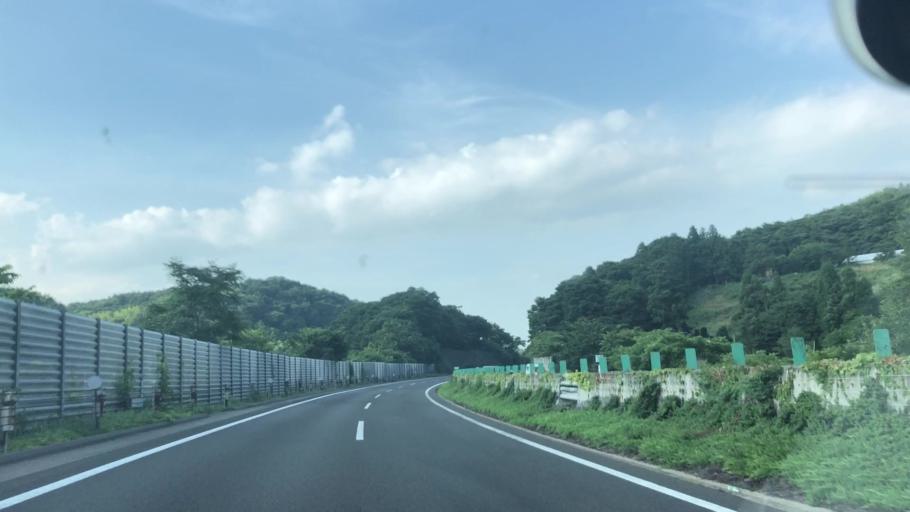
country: JP
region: Miyagi
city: Shiroishi
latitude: 37.9350
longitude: 140.6089
